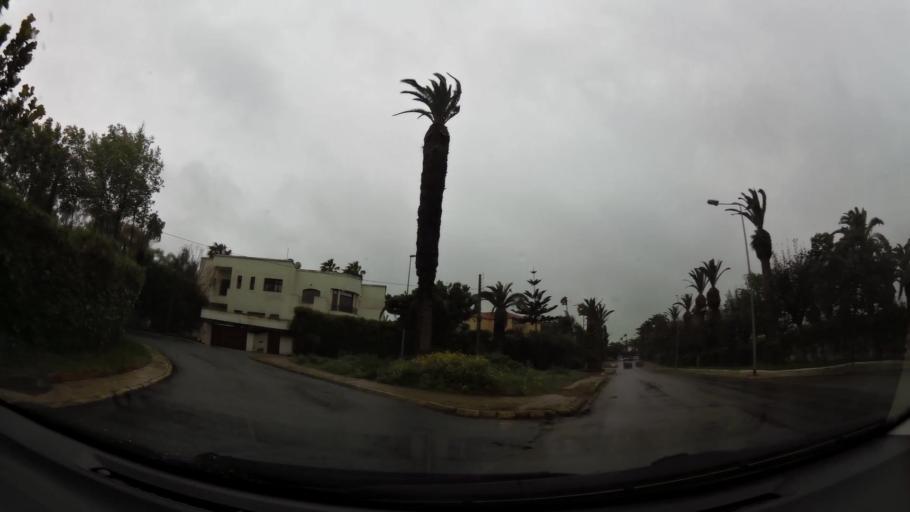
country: MA
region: Grand Casablanca
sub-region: Casablanca
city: Casablanca
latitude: 33.5907
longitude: -7.6638
